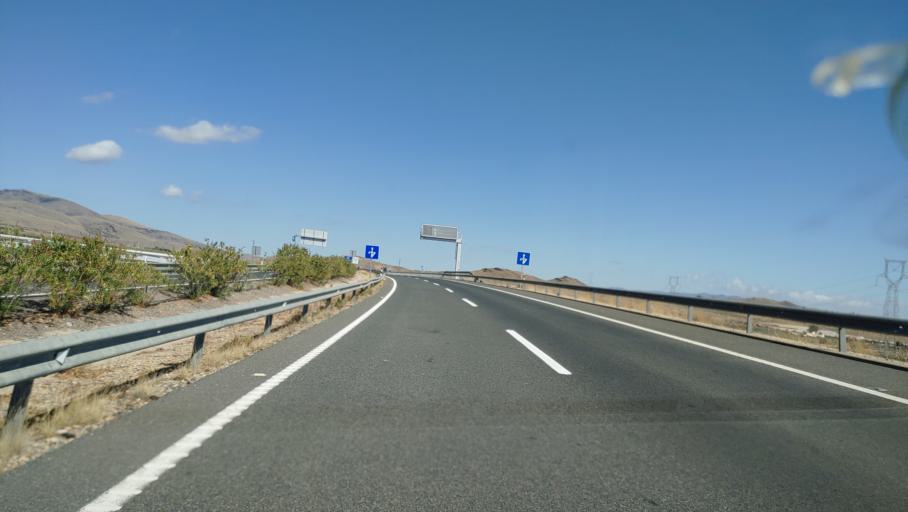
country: ES
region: Andalusia
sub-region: Provincia de Almeria
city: Gergal
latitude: 37.1179
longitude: -2.6014
